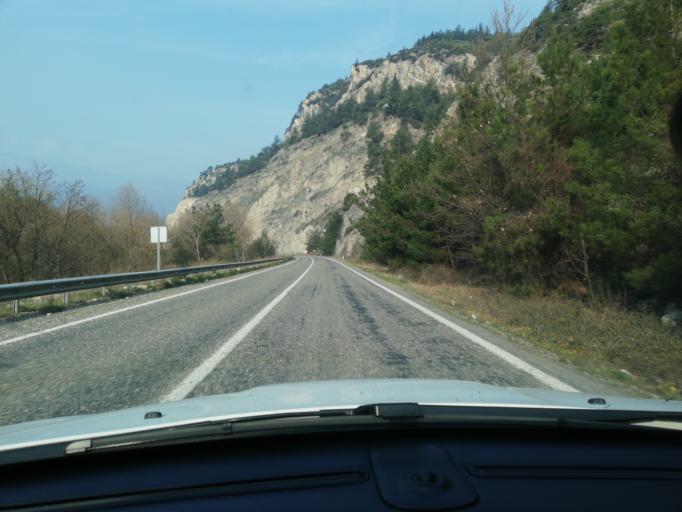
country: TR
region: Karabuk
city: Karabuk
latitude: 41.1601
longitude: 32.5574
